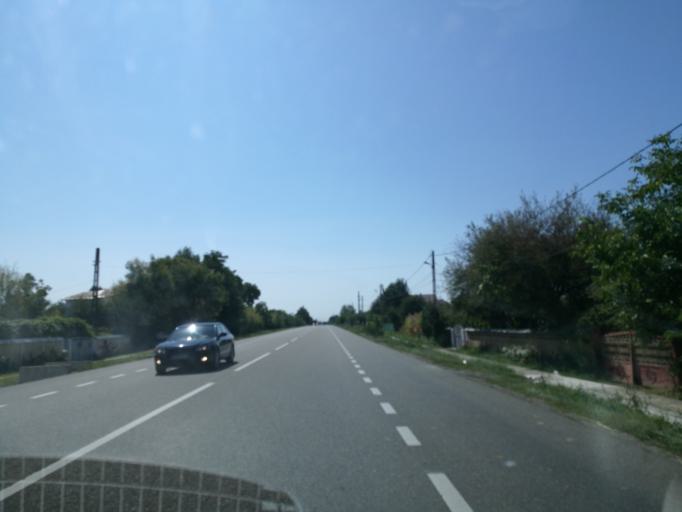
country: RO
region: Bacau
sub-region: Comuna Filipesti
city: Filipesti
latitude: 46.7389
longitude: 26.8858
